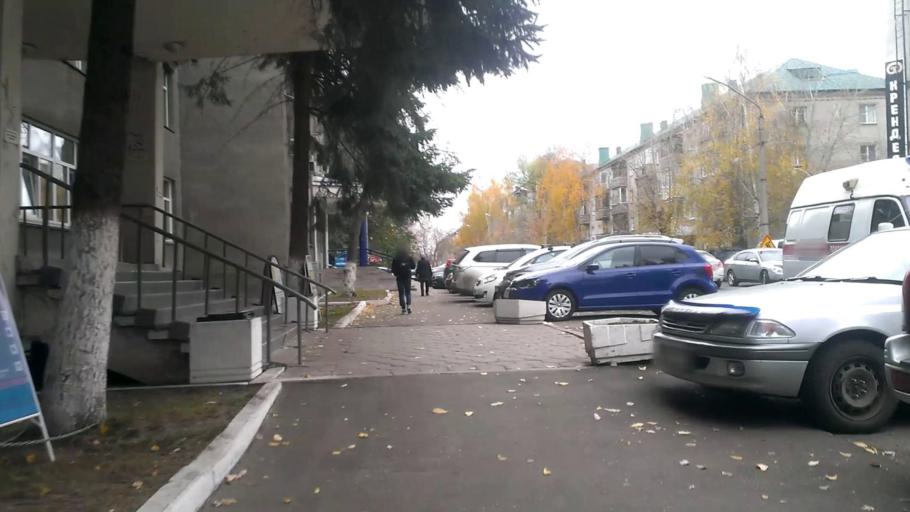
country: RU
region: Altai Krai
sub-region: Gorod Barnaulskiy
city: Barnaul
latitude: 53.3493
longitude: 83.7712
